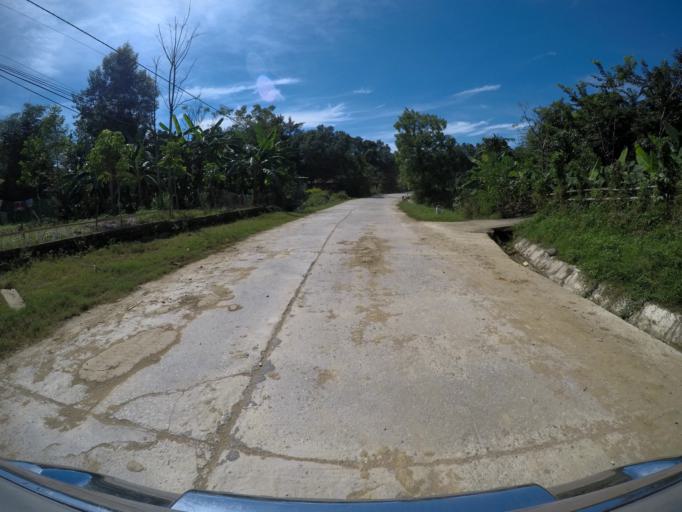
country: VN
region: Quang Nam
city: Thanh My
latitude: 15.6660
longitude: 107.7111
